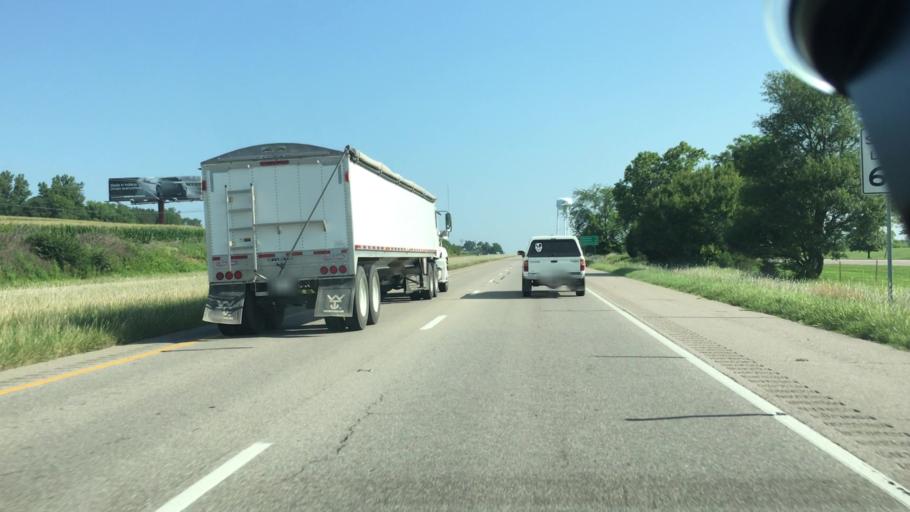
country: US
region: Indiana
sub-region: Gibson County
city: Fort Branch
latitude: 38.2835
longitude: -87.5675
